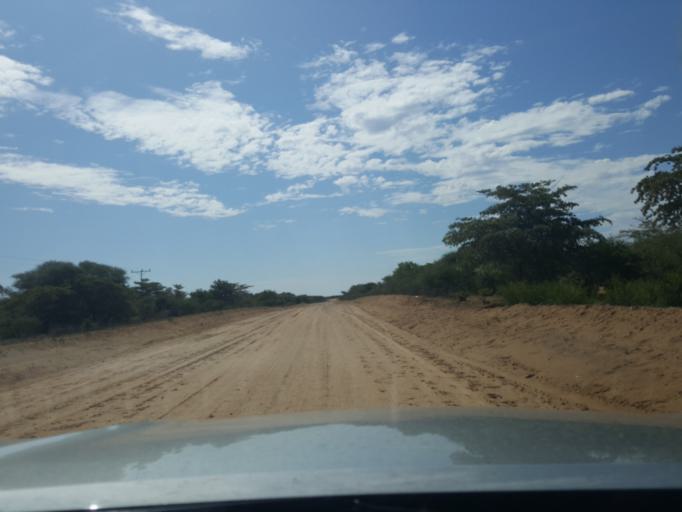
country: BW
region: Kweneng
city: Khudumelapye
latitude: -23.8671
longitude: 24.8927
